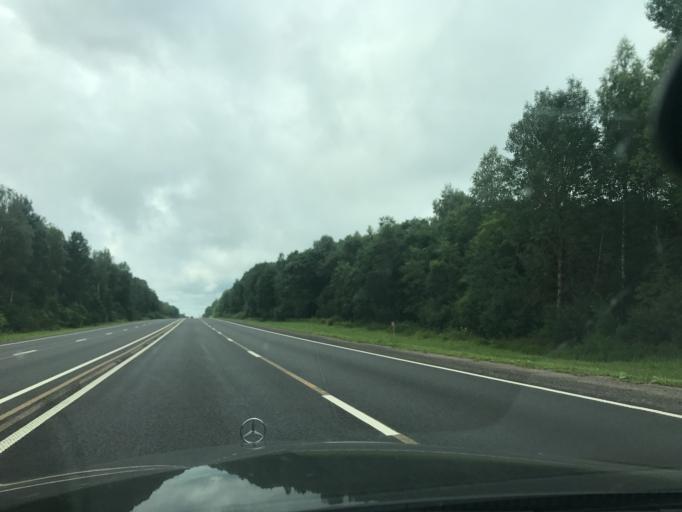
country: RU
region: Smolensk
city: Katyn'
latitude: 54.7706
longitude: 31.5326
